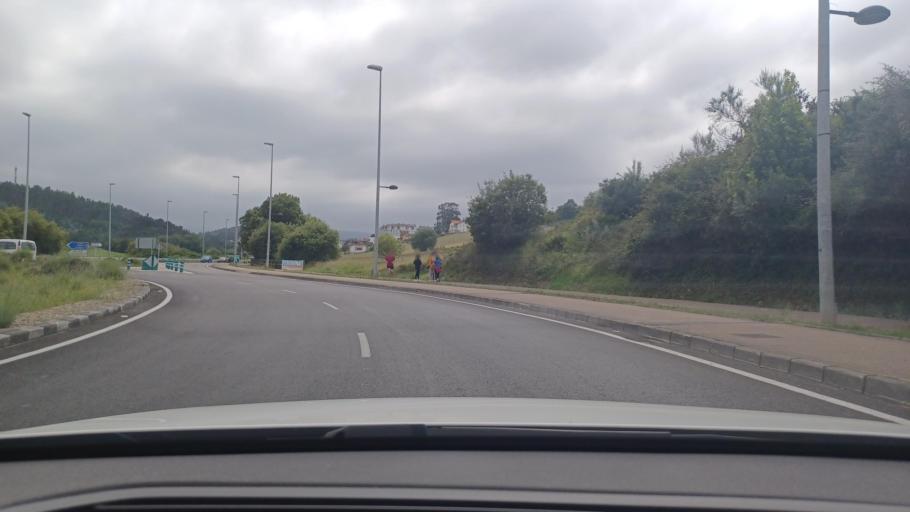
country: ES
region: Asturias
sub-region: Province of Asturias
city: Castrillon
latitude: 43.5661
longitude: -5.9662
